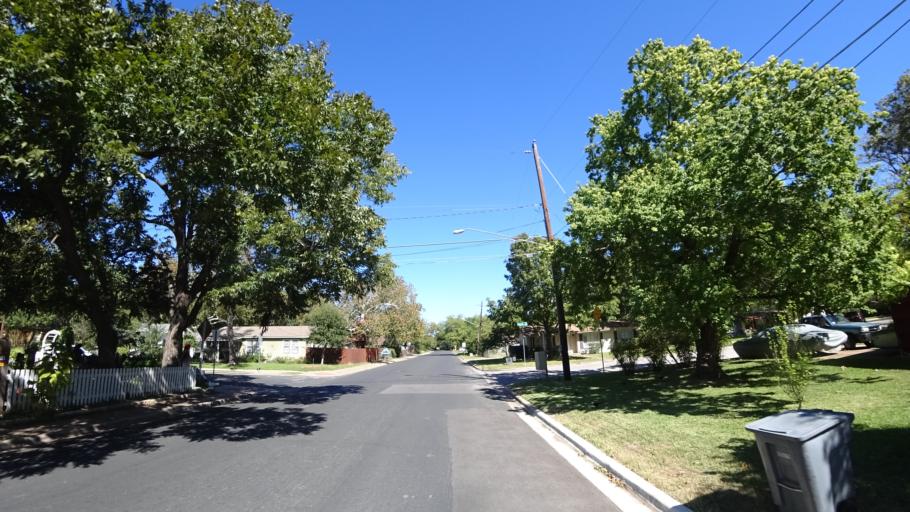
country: US
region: Texas
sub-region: Travis County
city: Austin
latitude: 30.3325
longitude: -97.7271
